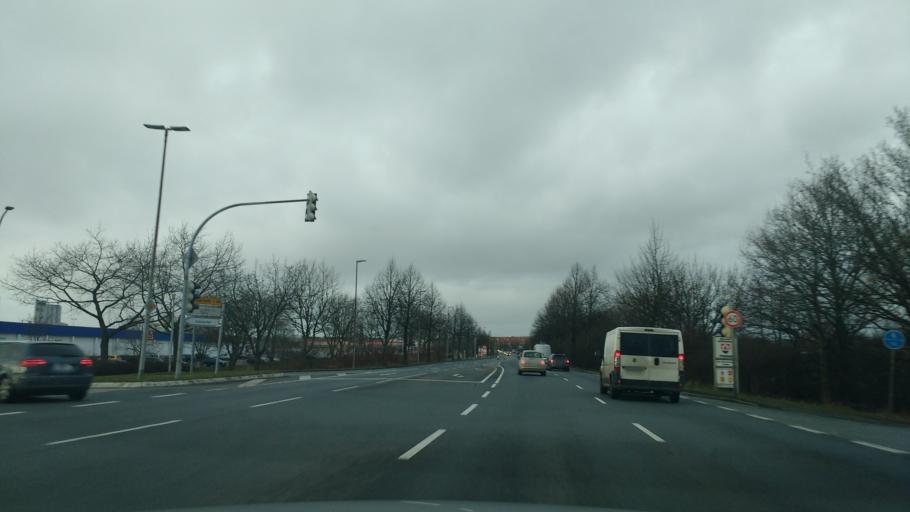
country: DE
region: Schleswig-Holstein
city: Itzehoe
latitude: 53.9130
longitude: 9.5161
